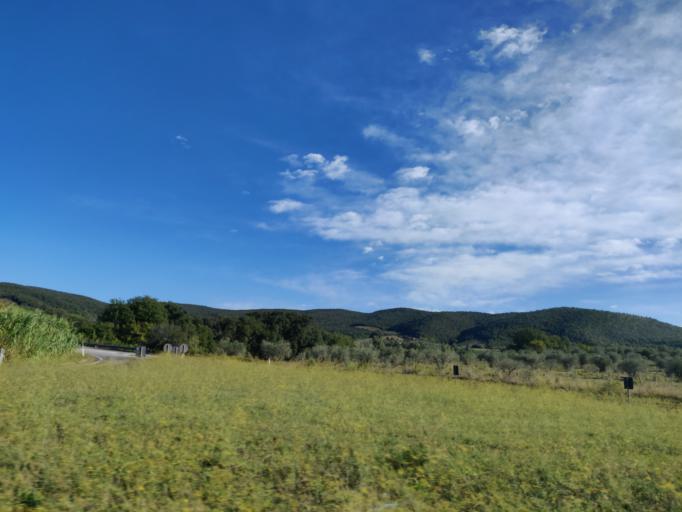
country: IT
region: Tuscany
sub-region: Provincia di Grosseto
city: Gavorrano
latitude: 42.9504
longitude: 10.8844
